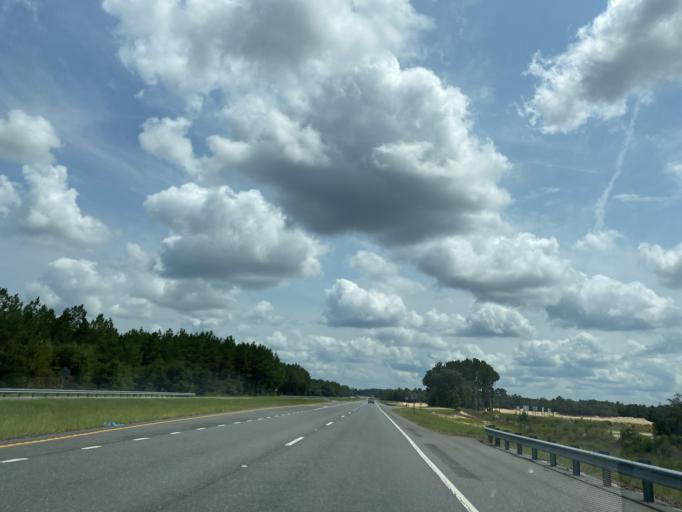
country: US
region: Georgia
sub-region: Ware County
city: Deenwood
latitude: 31.3096
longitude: -82.4559
